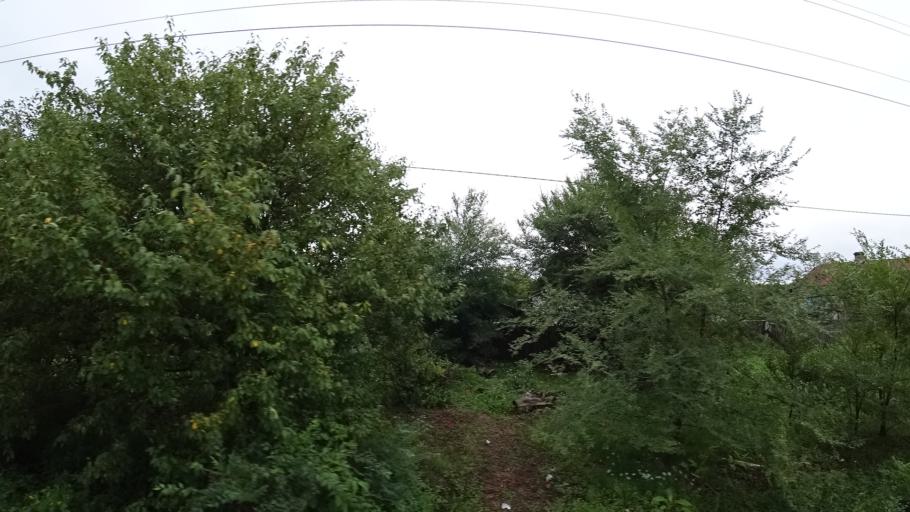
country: RU
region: Primorskiy
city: Chernigovka
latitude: 44.3423
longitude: 132.5859
